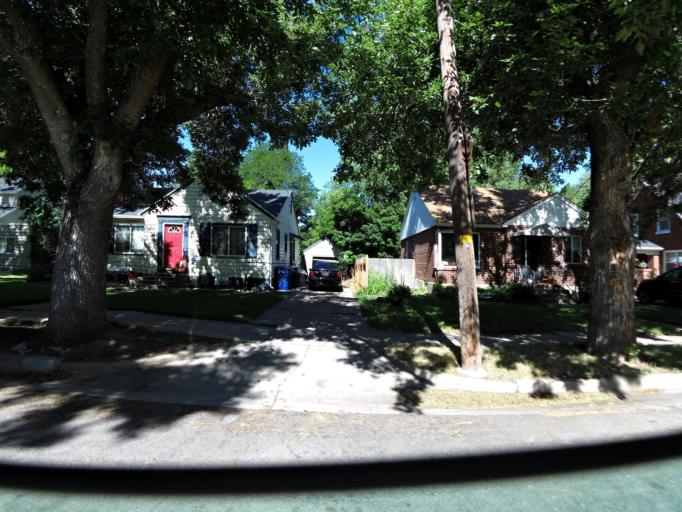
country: US
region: Utah
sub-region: Weber County
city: Ogden
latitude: 41.2166
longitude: -111.9456
